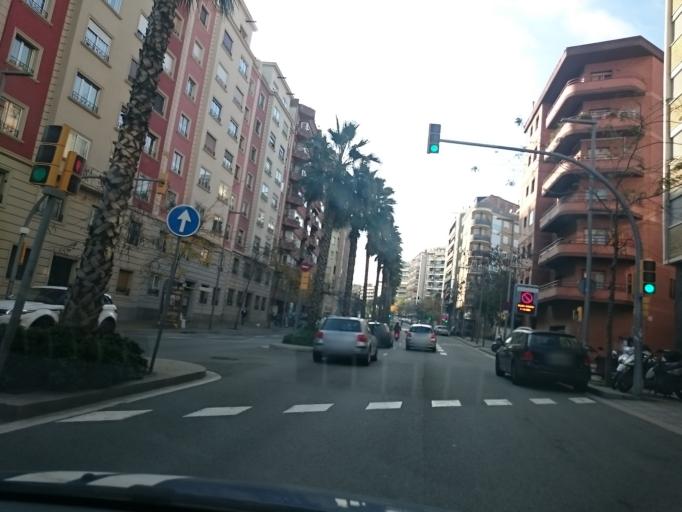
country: ES
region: Catalonia
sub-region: Provincia de Barcelona
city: Sarria-Sant Gervasi
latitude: 41.4059
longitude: 2.1469
